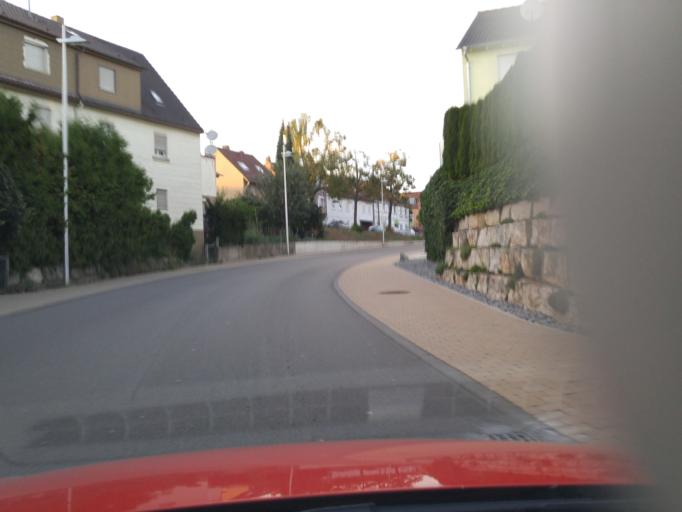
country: DE
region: Baden-Wuerttemberg
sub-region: Regierungsbezirk Stuttgart
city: Untereisesheim
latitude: 49.1951
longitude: 9.2019
